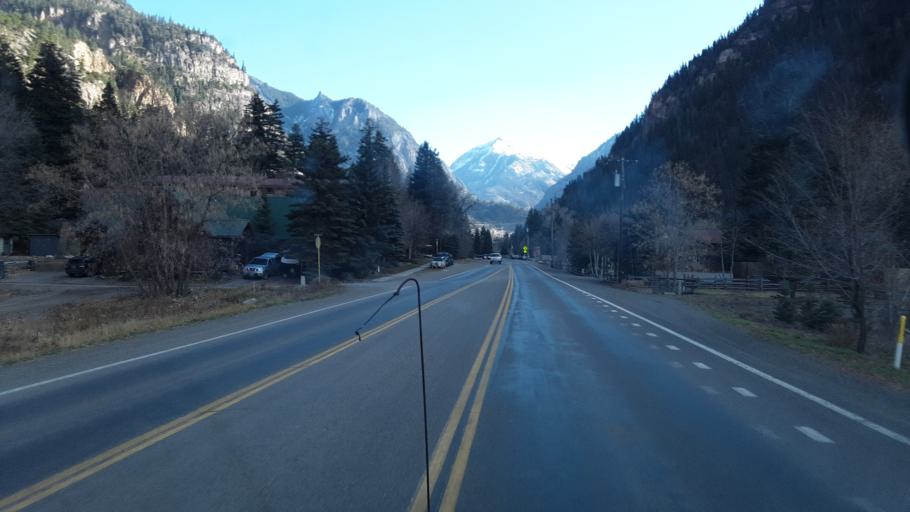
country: US
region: Colorado
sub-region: Ouray County
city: Ouray
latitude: 38.0383
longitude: -107.6789
